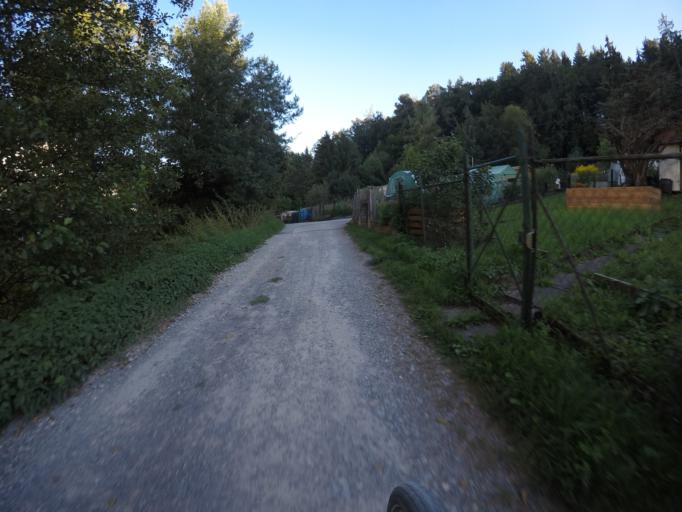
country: DE
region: Baden-Wuerttemberg
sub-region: Regierungsbezirk Stuttgart
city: Waldenbuch
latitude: 48.6376
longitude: 9.1221
